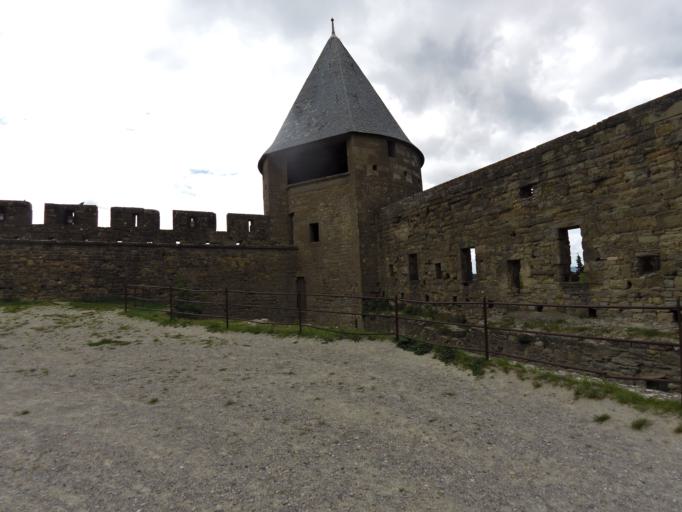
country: FR
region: Languedoc-Roussillon
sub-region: Departement de l'Aude
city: Carcassonne
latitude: 43.2046
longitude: 2.3618
